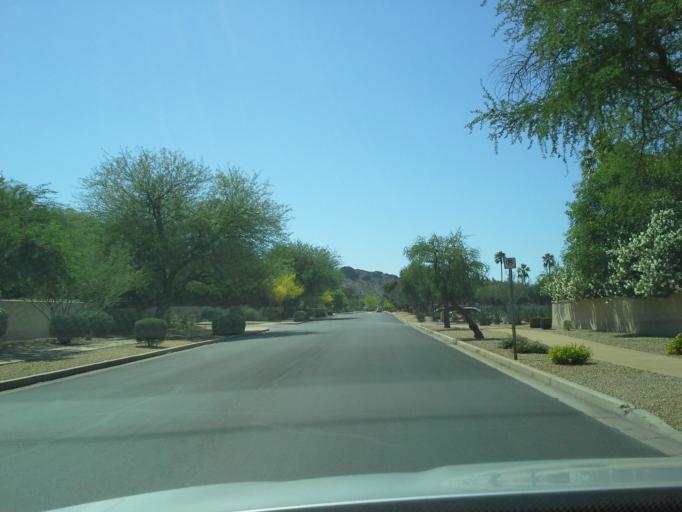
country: US
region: Arizona
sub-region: Maricopa County
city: Paradise Valley
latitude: 33.5531
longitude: -111.9329
